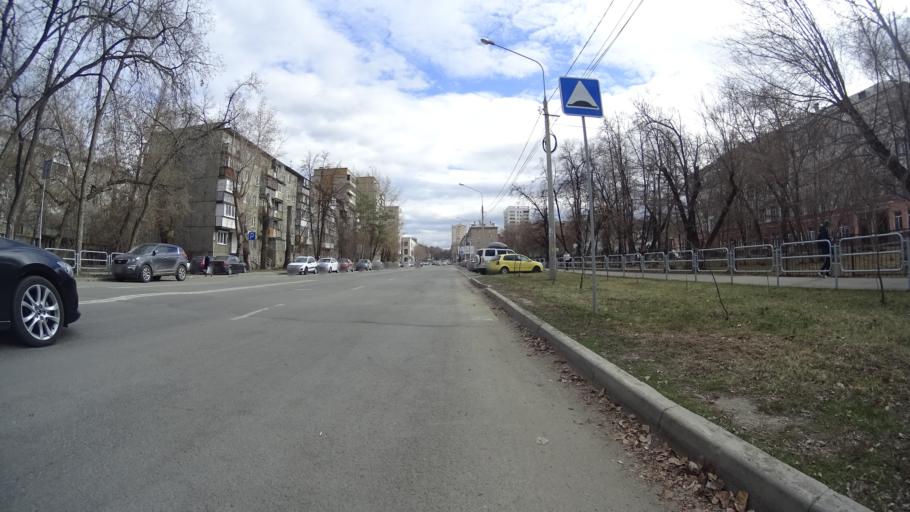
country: RU
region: Chelyabinsk
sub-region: Gorod Chelyabinsk
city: Chelyabinsk
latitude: 55.1642
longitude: 61.3860
